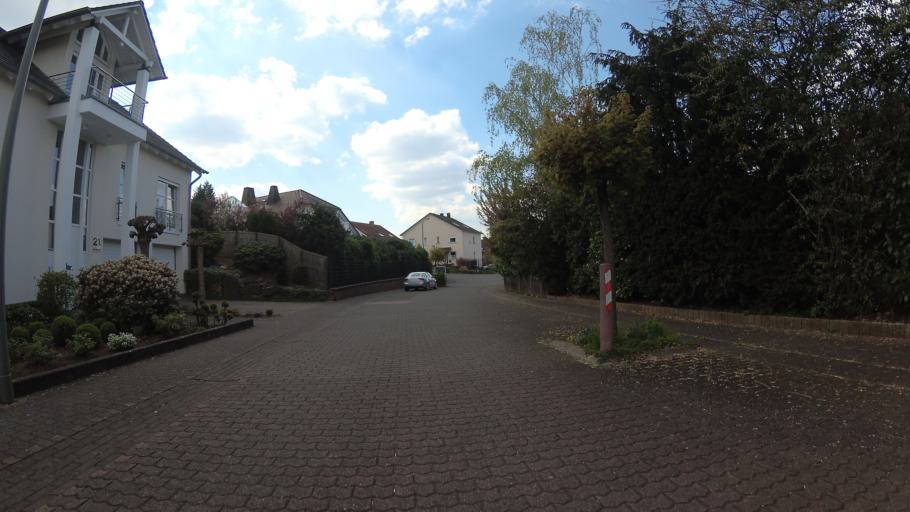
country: DE
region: Saarland
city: Riegelsberg
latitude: 49.3070
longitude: 6.9337
